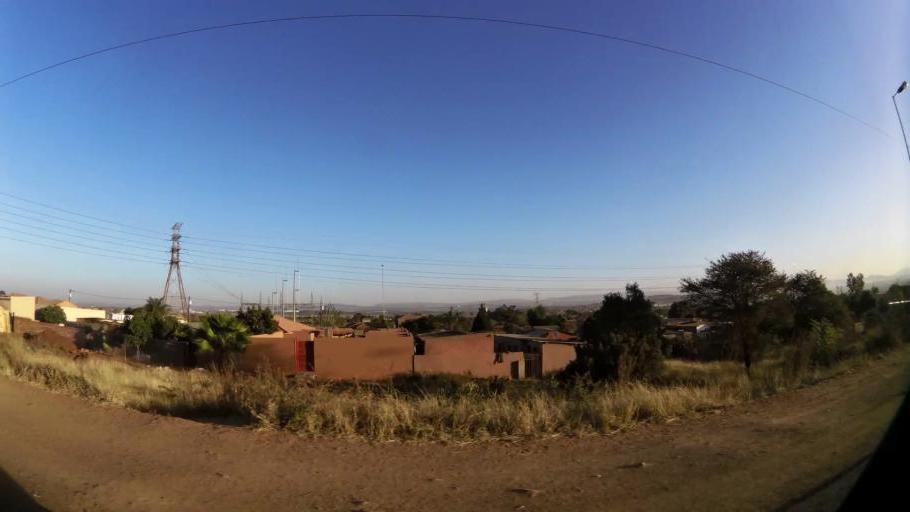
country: ZA
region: Gauteng
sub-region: City of Tshwane Metropolitan Municipality
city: Mabopane
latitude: -25.5760
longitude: 28.0778
